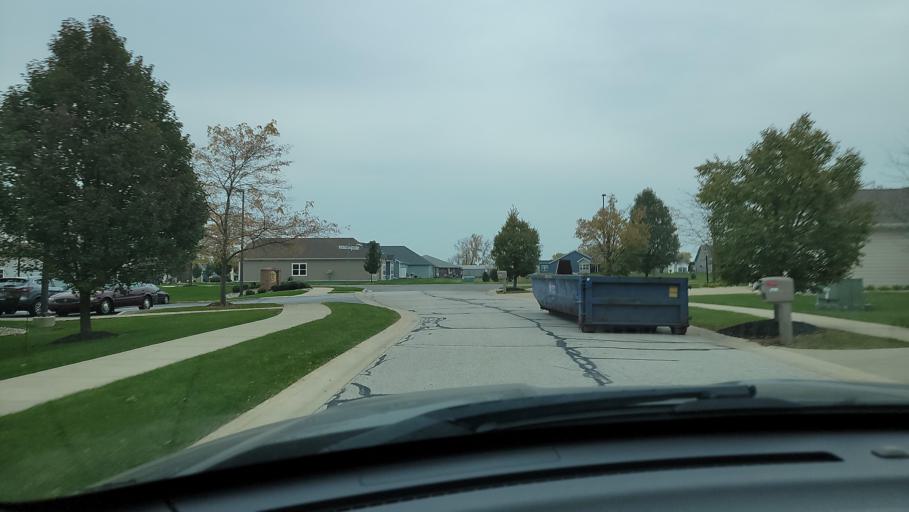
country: US
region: Indiana
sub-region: Porter County
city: Portage
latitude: 41.5448
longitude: -87.1722
